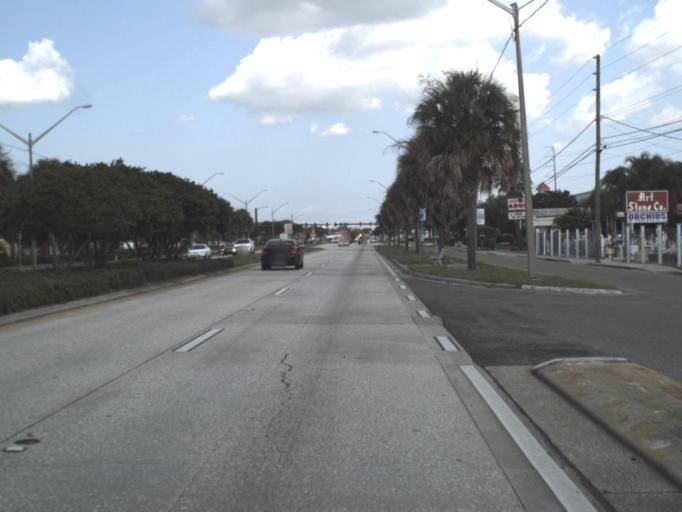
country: US
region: Florida
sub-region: Pinellas County
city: Kenneth City
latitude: 27.8046
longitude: -82.7465
